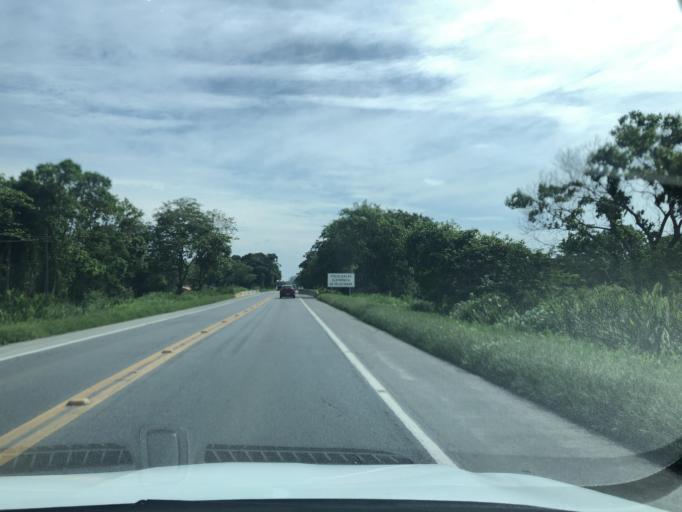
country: BR
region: Santa Catarina
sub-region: Sao Francisco Do Sul
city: Sao Francisco do Sul
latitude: -26.3261
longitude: -48.6498
